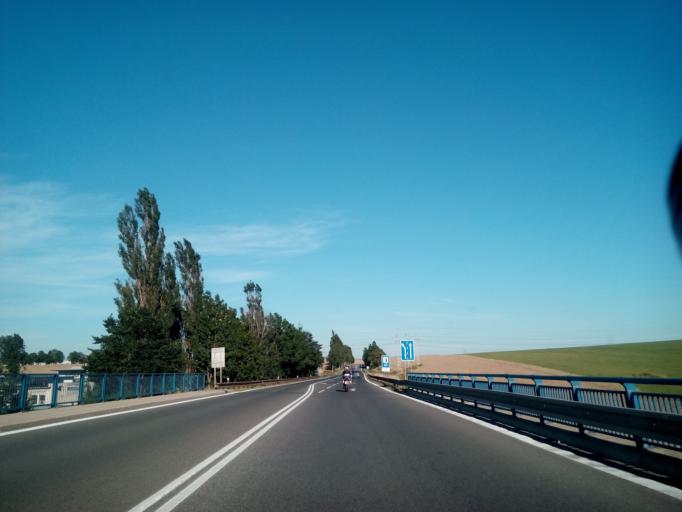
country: SK
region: Presovsky
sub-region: Okres Poprad
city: Poprad
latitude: 49.0496
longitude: 20.3088
